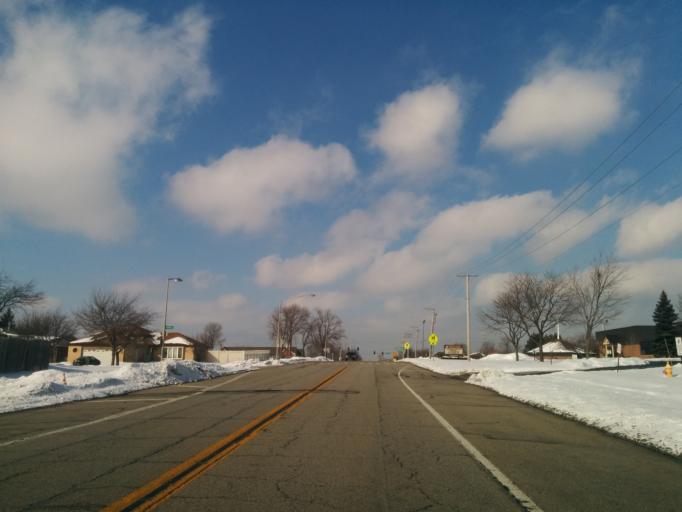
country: US
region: Illinois
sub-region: Cook County
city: Orland Hills
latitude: 41.5773
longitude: -87.8226
